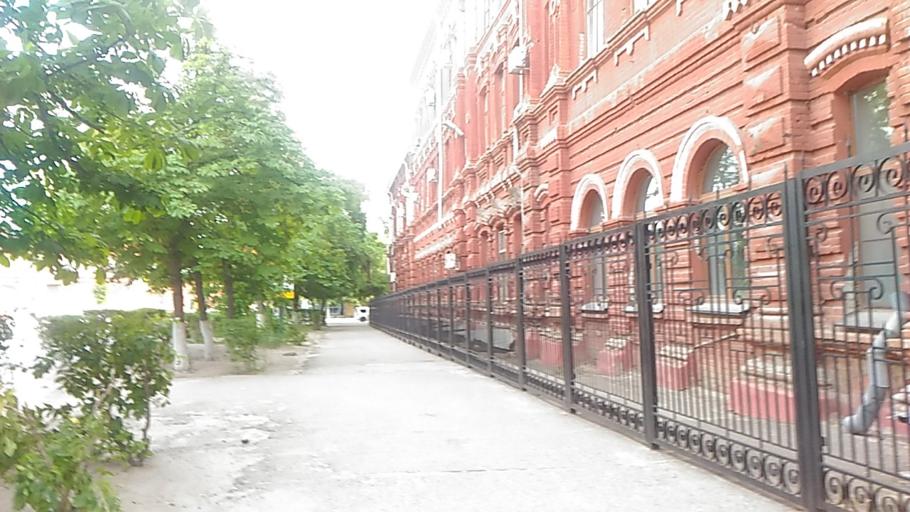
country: RU
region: Volgograd
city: Volgograd
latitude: 48.6943
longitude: 44.4984
